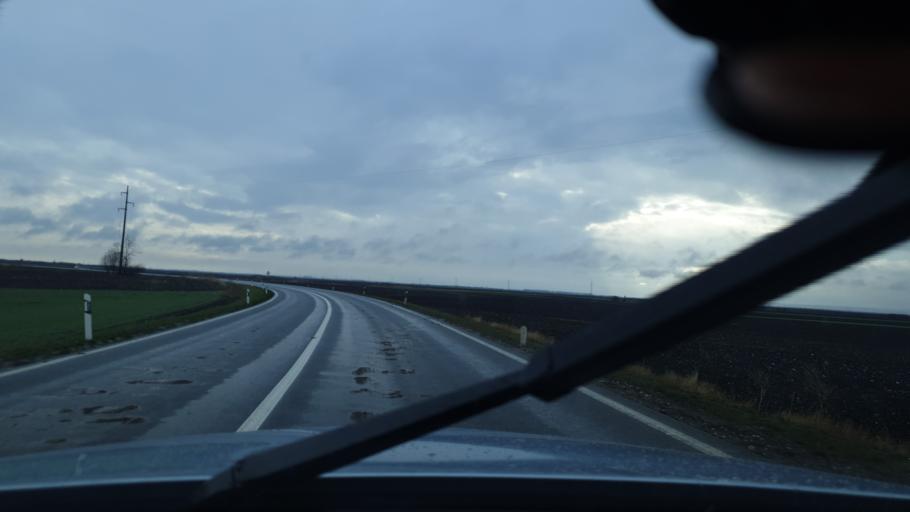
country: RS
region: Autonomna Pokrajina Vojvodina
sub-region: Juznobanatski Okrug
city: Kovin
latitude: 44.8109
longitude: 20.8581
